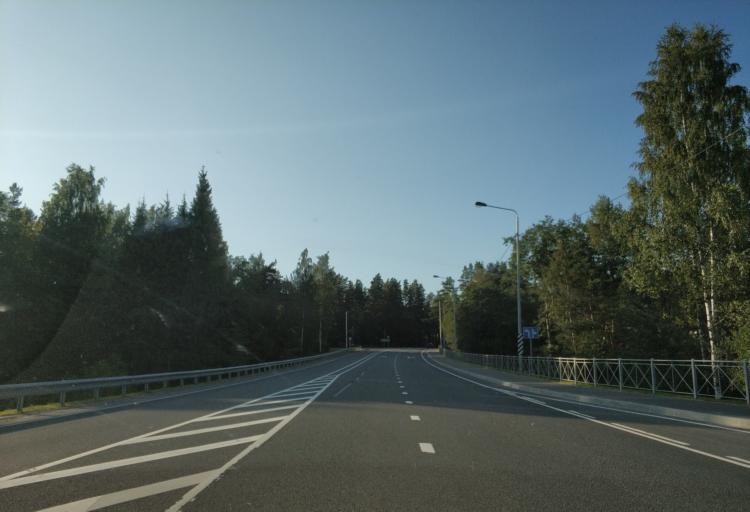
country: RU
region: Leningrad
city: Sapernoye
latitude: 60.7045
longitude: 29.9692
